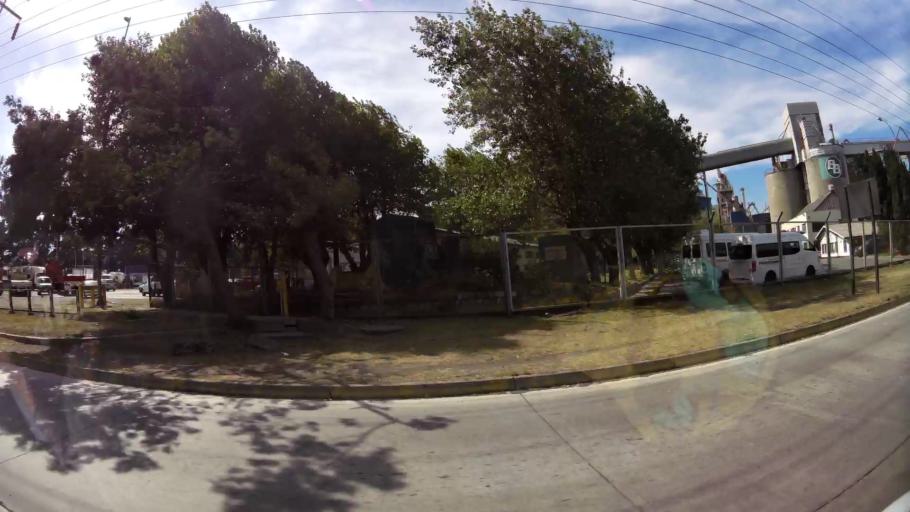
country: CL
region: Biobio
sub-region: Provincia de Concepcion
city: Talcahuano
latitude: -36.7419
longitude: -73.1197
